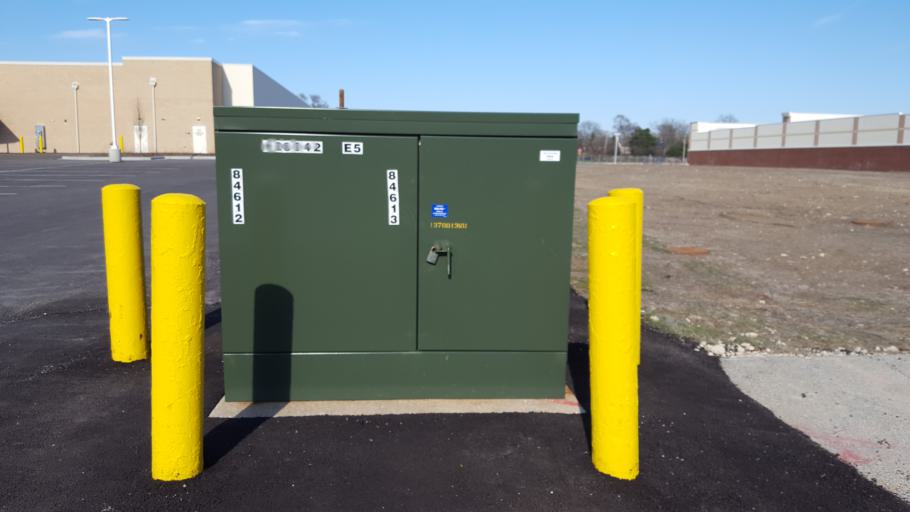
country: US
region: Illinois
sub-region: Cook County
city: Northbrook
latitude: 42.1492
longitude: -87.8361
